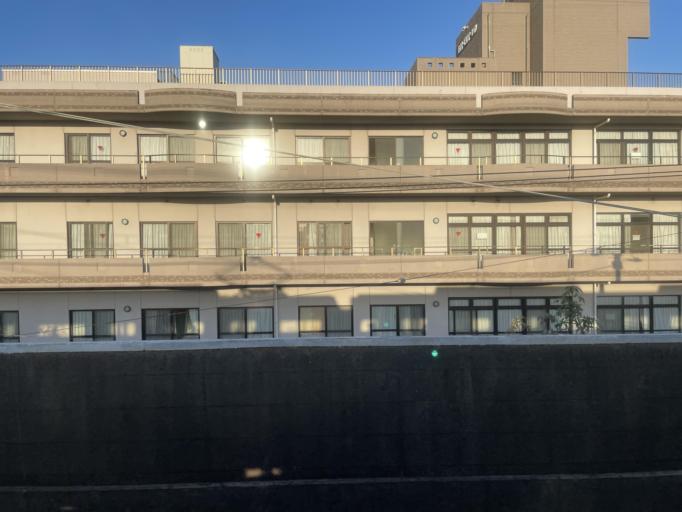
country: JP
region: Osaka
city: Matsubara
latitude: 34.6021
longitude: 135.5325
